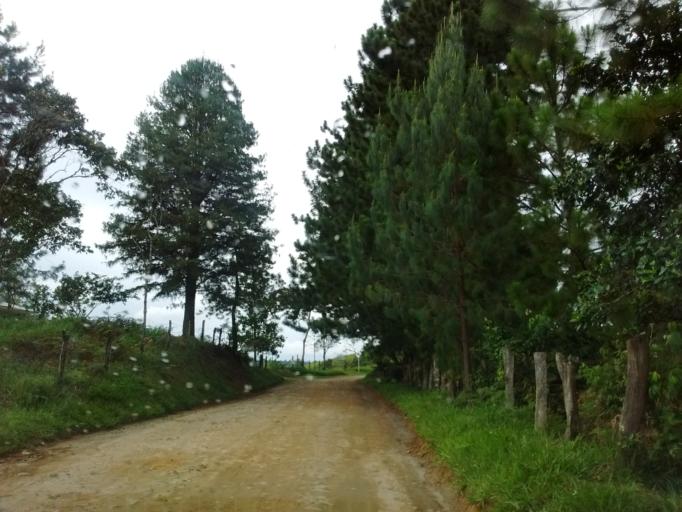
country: CO
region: Cauca
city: Cajibio
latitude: 2.5839
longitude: -76.6772
